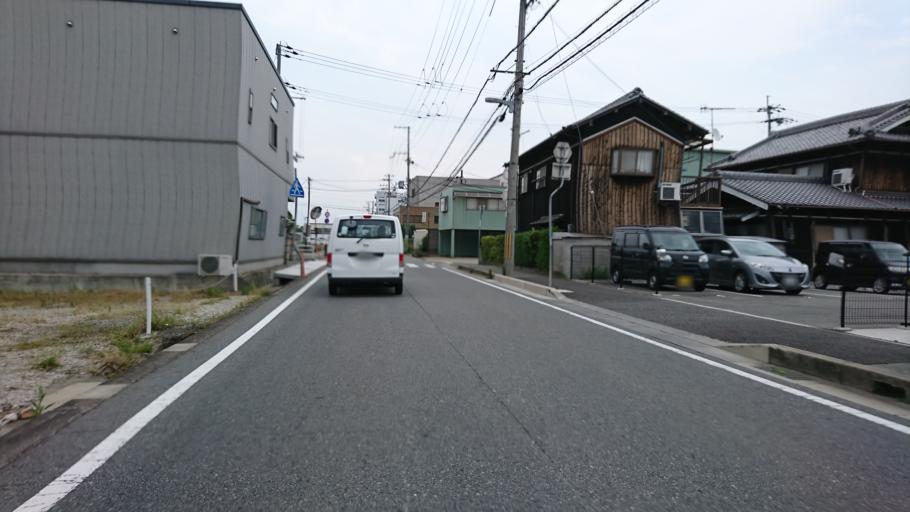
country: JP
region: Hyogo
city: Miki
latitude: 34.7299
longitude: 134.9173
